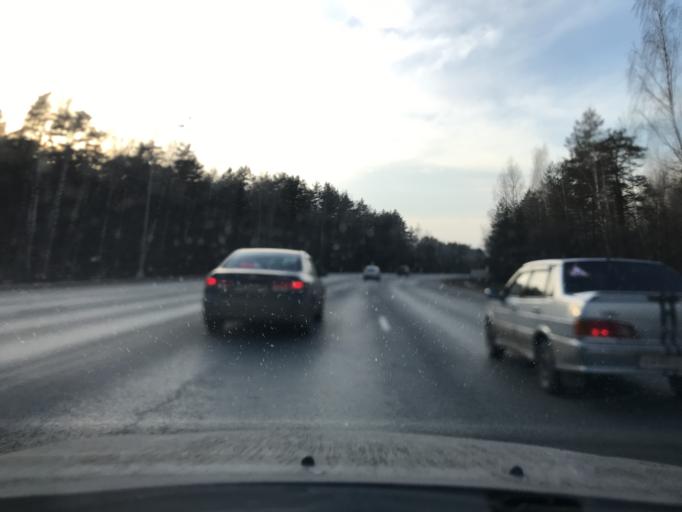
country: RU
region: Kaluga
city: Mstikhino
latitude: 54.5250
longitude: 36.1824
